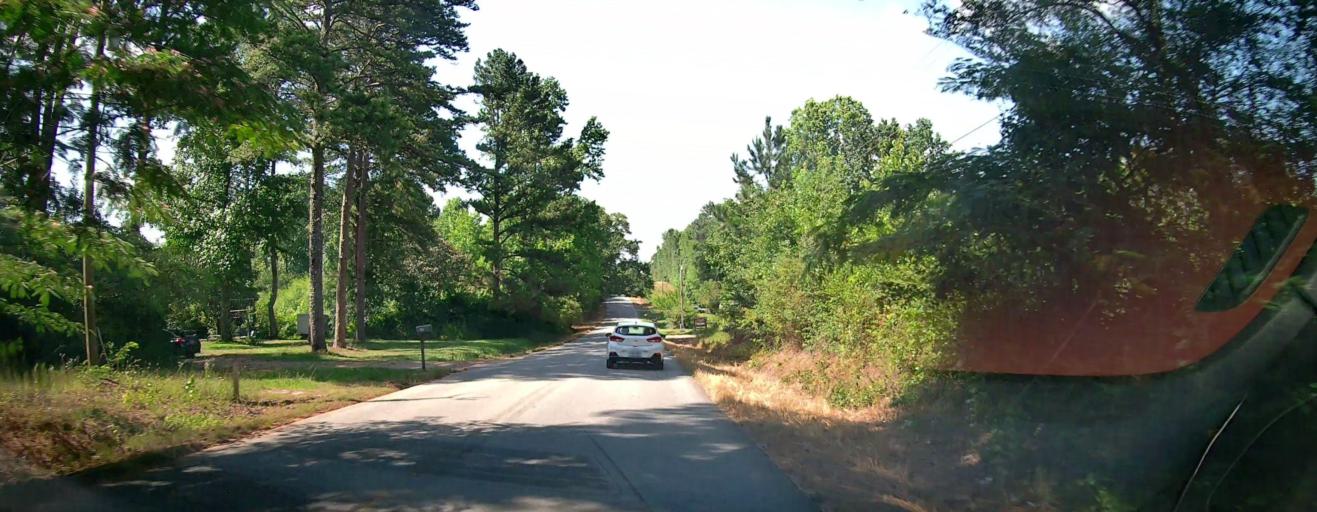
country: US
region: Georgia
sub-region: Spalding County
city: East Griffin
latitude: 33.2580
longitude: -84.1901
